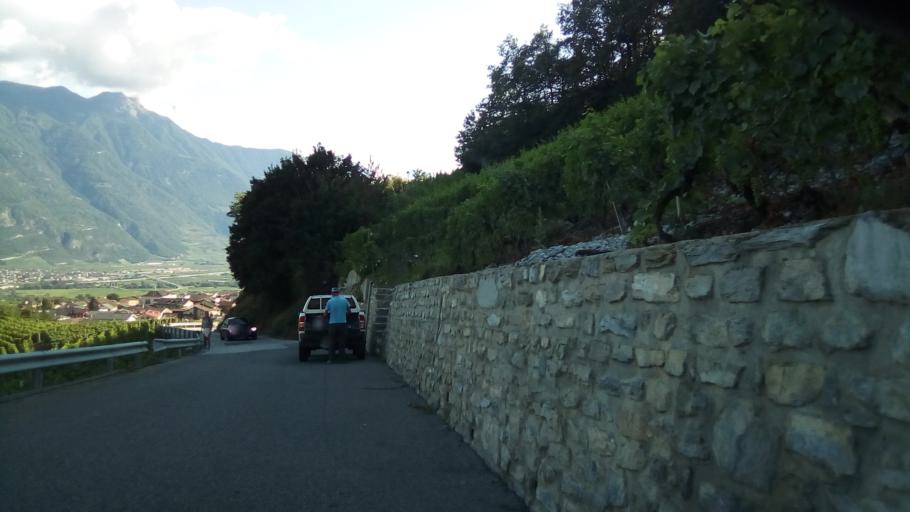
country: CH
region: Valais
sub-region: Conthey District
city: Chamoson
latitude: 46.2067
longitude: 7.2251
